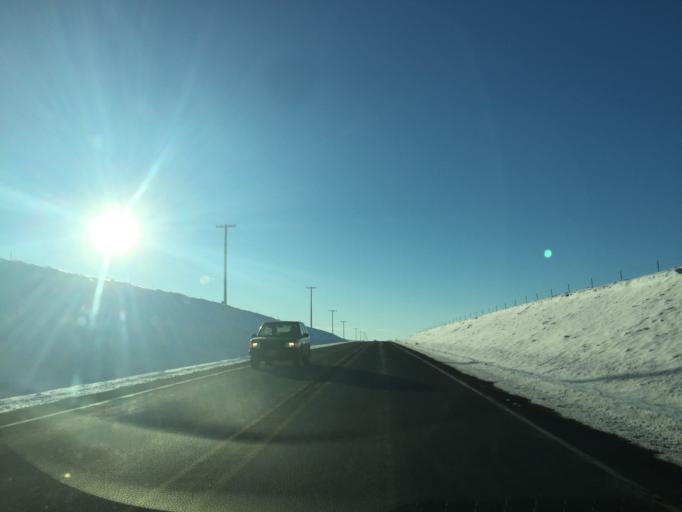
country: US
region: Washington
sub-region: Okanogan County
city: Coulee Dam
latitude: 47.7353
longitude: -118.8547
